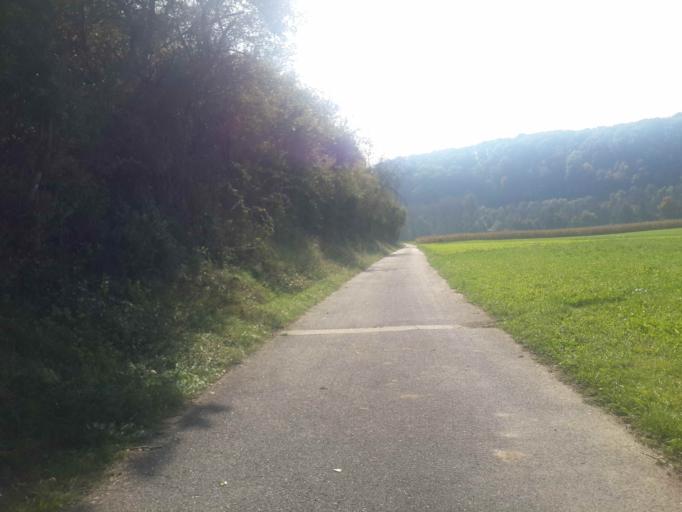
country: DE
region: Baden-Wuerttemberg
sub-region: Regierungsbezirk Stuttgart
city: Neudenau
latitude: 49.2956
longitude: 9.3188
